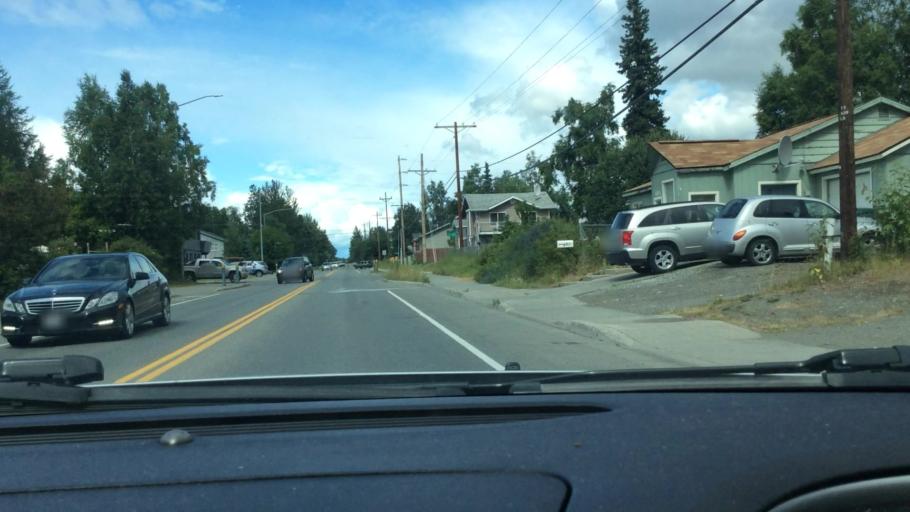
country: US
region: Alaska
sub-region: Anchorage Municipality
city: Elmendorf Air Force Base
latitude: 61.2122
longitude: -149.7559
